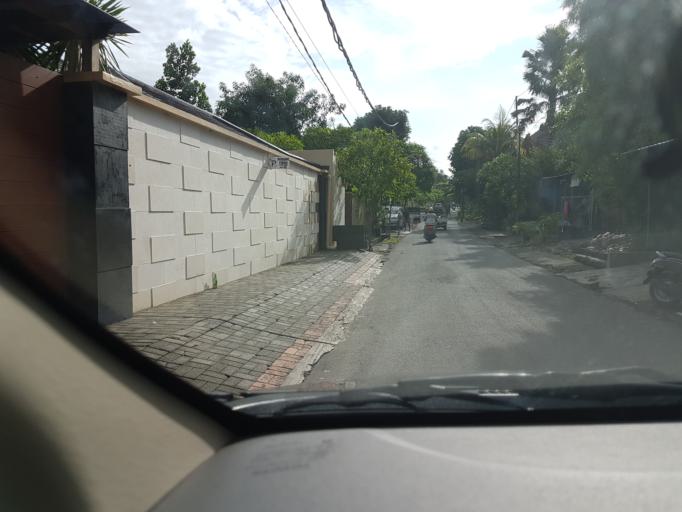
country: ID
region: Bali
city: Kuta
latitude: -8.6831
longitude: 115.1750
